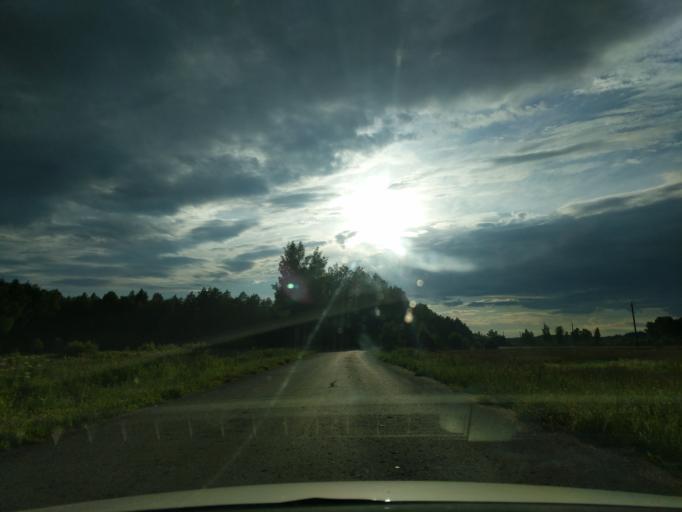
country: RU
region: Kaluga
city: Myatlevo
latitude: 54.8074
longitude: 35.6902
